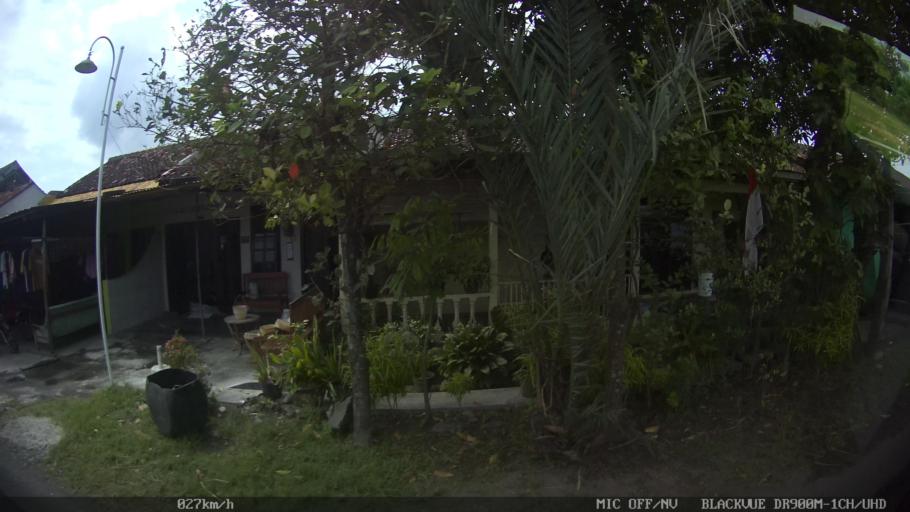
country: ID
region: Daerah Istimewa Yogyakarta
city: Depok
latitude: -7.8169
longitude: 110.4429
